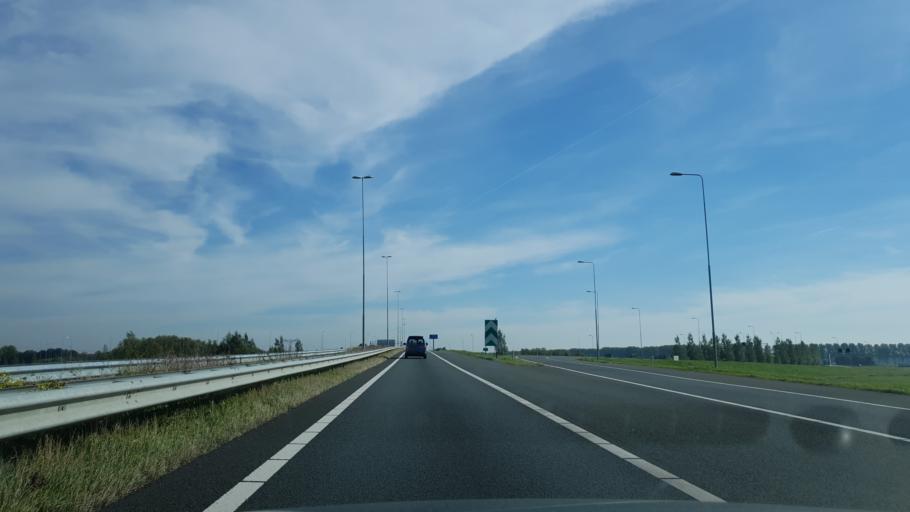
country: NL
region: Gelderland
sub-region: Gemeente Wijchen
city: Bergharen
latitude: 51.8602
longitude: 5.7053
